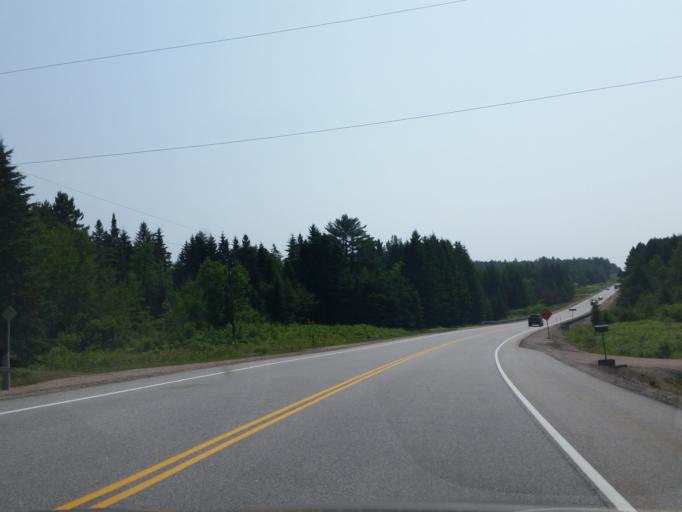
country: CA
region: Ontario
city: Mattawa
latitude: 46.3045
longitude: -78.5741
